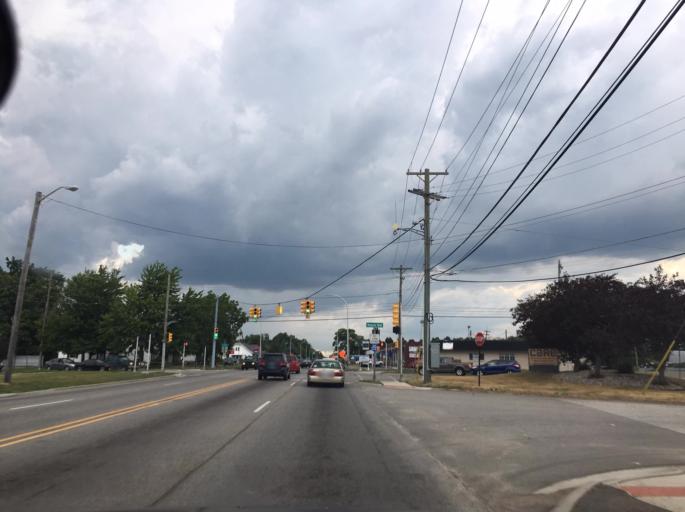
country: US
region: Michigan
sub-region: Macomb County
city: Fraser
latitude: 42.5311
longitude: -82.9482
